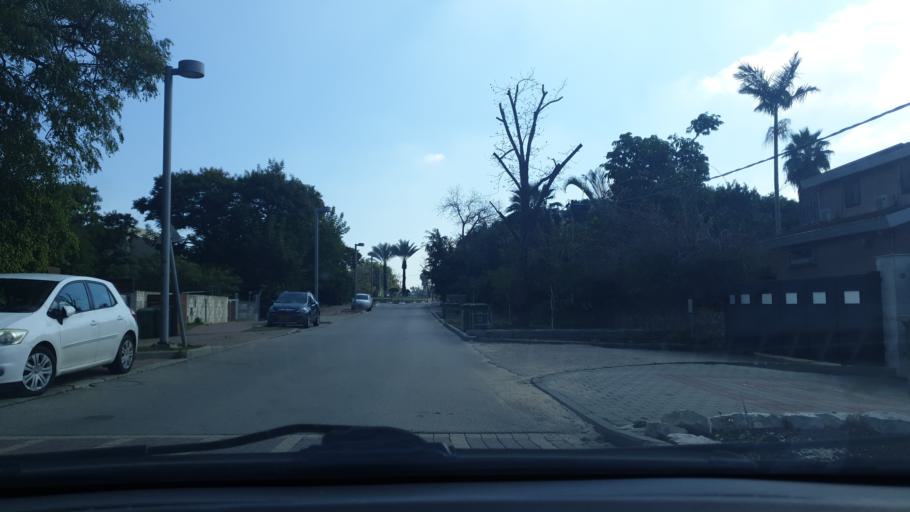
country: IL
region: Central District
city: Bet Dagan
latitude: 32.0085
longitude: 34.8193
